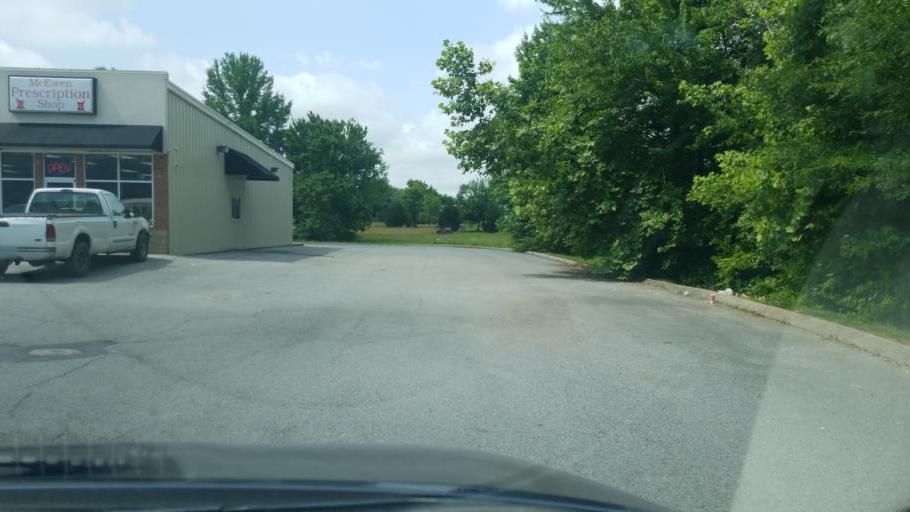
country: US
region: Tennessee
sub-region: Humphreys County
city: McEwen
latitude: 36.1052
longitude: -87.6260
